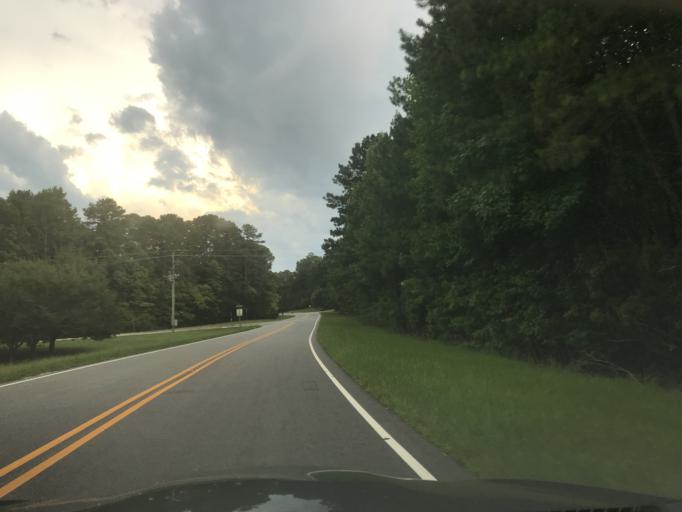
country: US
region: North Carolina
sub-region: Wake County
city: Wake Forest
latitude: 35.9422
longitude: -78.6099
